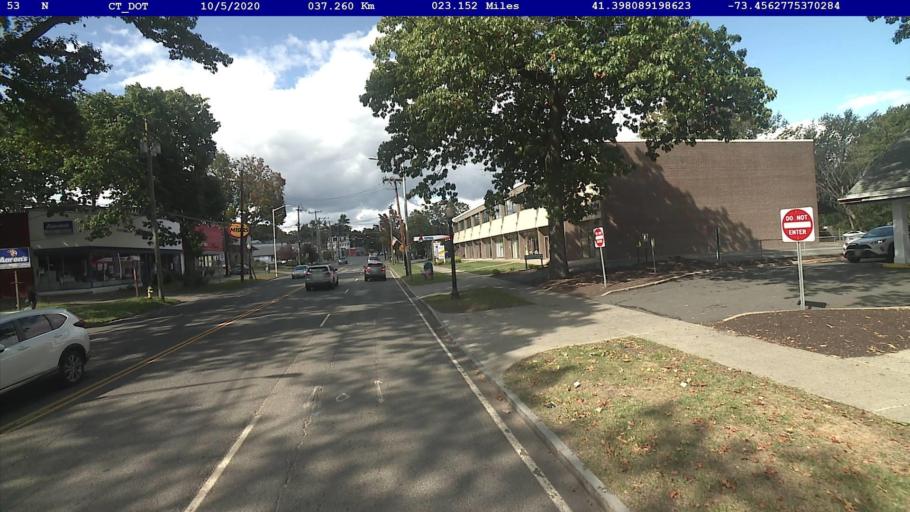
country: US
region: Connecticut
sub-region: Fairfield County
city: Danbury
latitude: 41.3982
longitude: -73.4562
